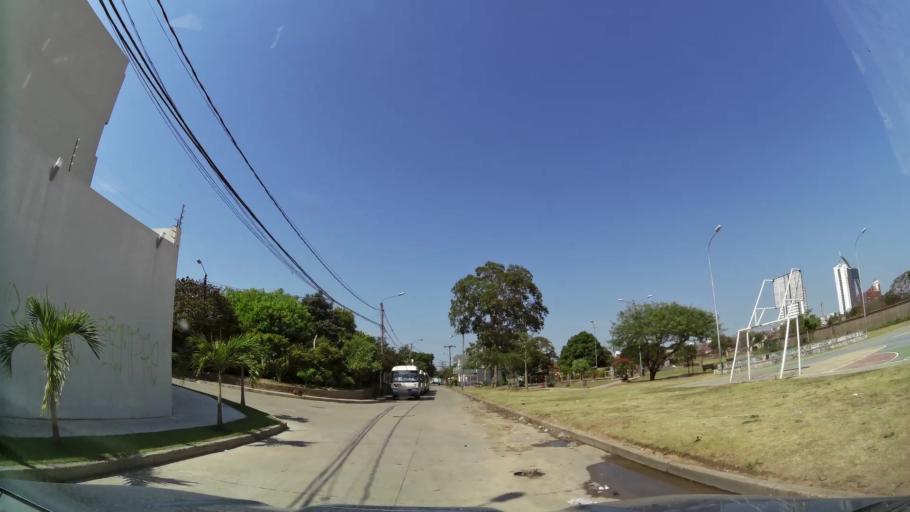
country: BO
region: Santa Cruz
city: Santa Cruz de la Sierra
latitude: -17.7502
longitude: -63.1955
